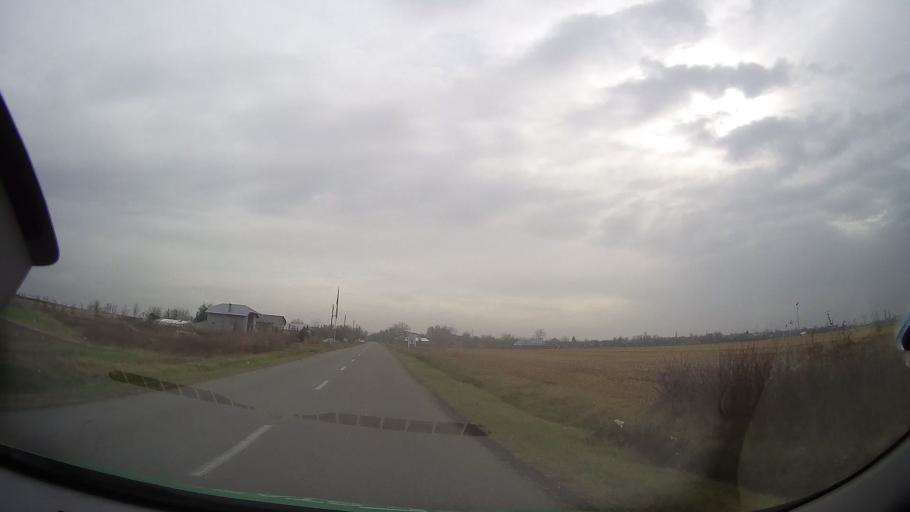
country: RO
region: Prahova
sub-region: Comuna Dumbrava
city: Dumbrava
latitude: 44.8796
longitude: 26.1817
